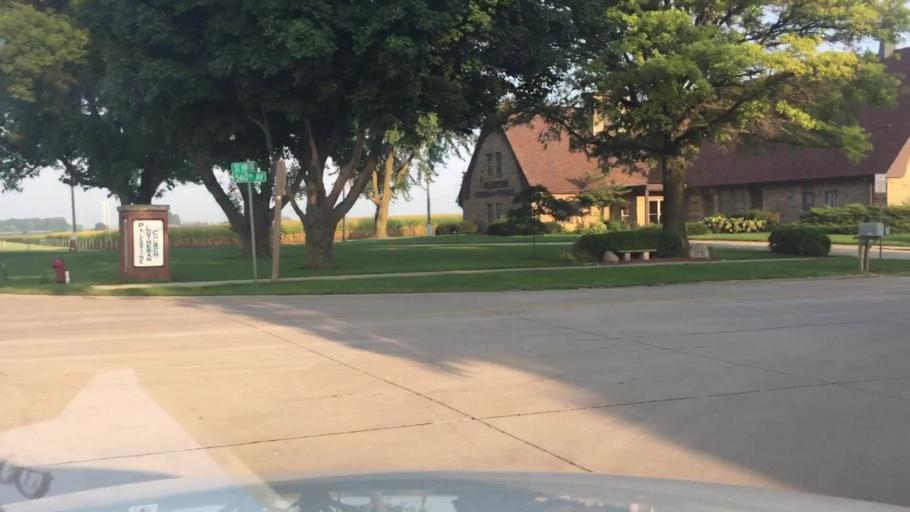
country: US
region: Iowa
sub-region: Story County
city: Huxley
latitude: 41.8779
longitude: -93.5809
